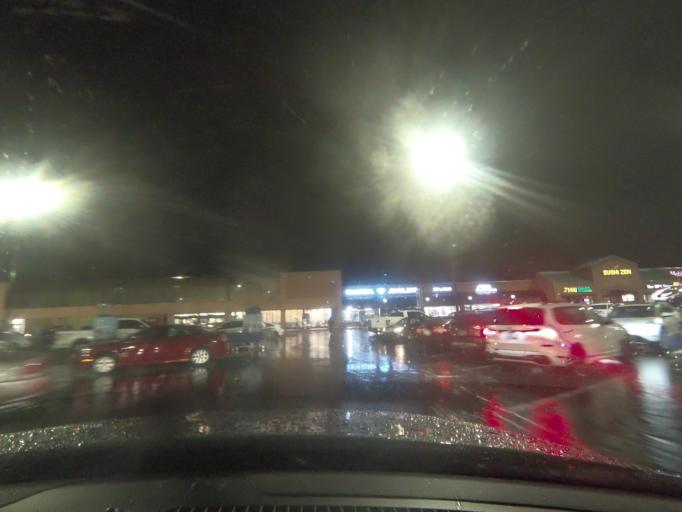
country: US
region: Georgia
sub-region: Cobb County
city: Acworth
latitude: 34.0356
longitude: -84.6768
